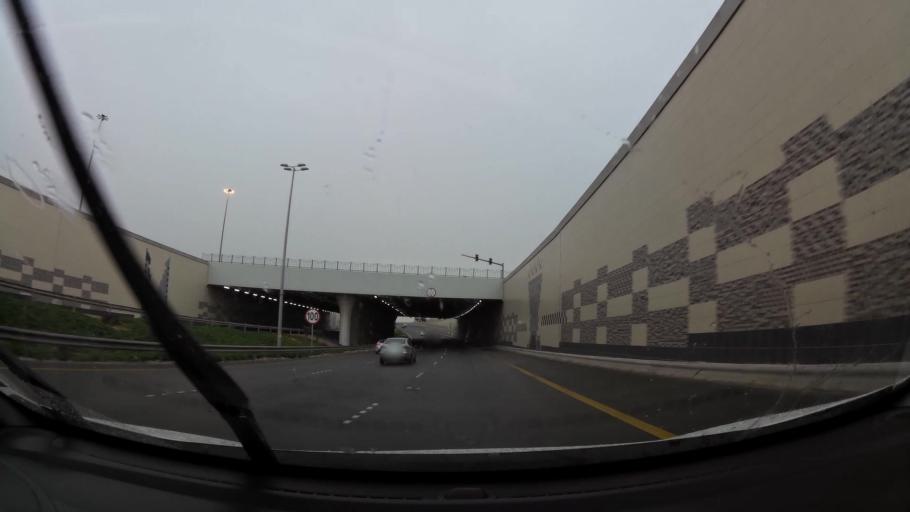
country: BH
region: Central Governorate
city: Madinat Hamad
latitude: 26.0986
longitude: 50.5112
